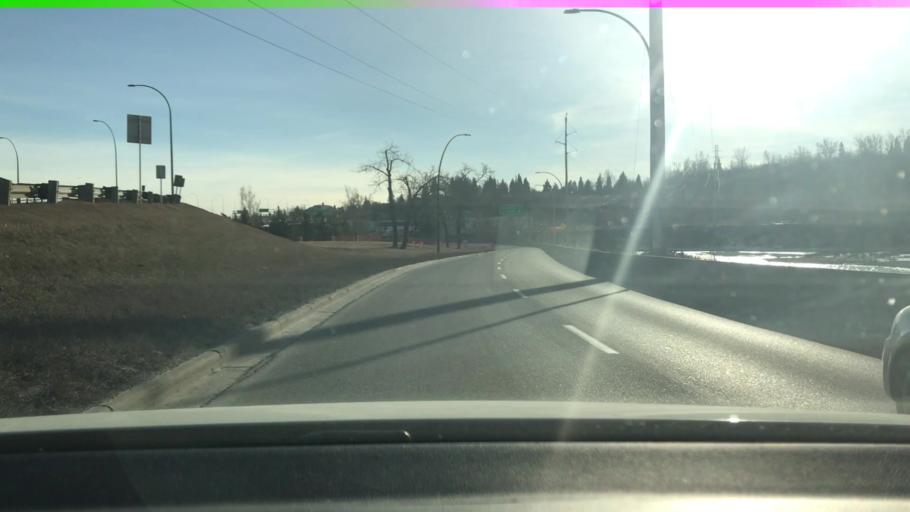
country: CA
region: Alberta
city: Calgary
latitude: 51.0505
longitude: -114.1188
